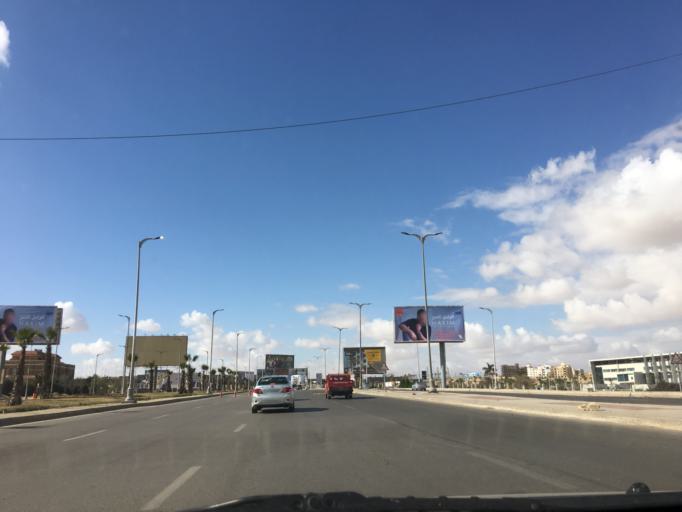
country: EG
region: Al Jizah
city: Awsim
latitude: 30.0090
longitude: 30.9883
